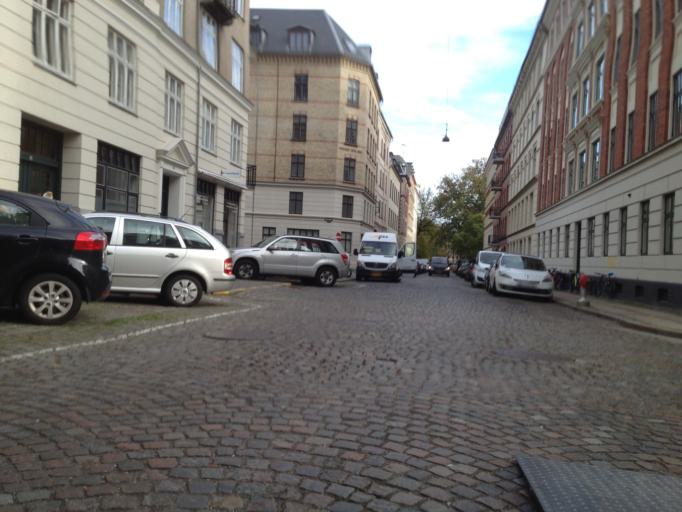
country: DK
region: Capital Region
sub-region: Kobenhavn
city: Copenhagen
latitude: 55.6992
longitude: 12.5806
